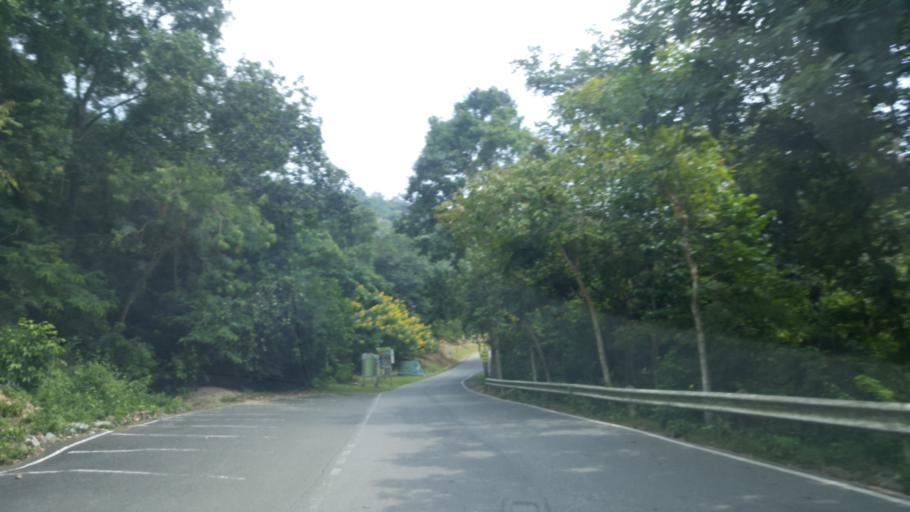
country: TH
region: Chon Buri
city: Ban Bueng
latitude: 13.2142
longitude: 101.0610
